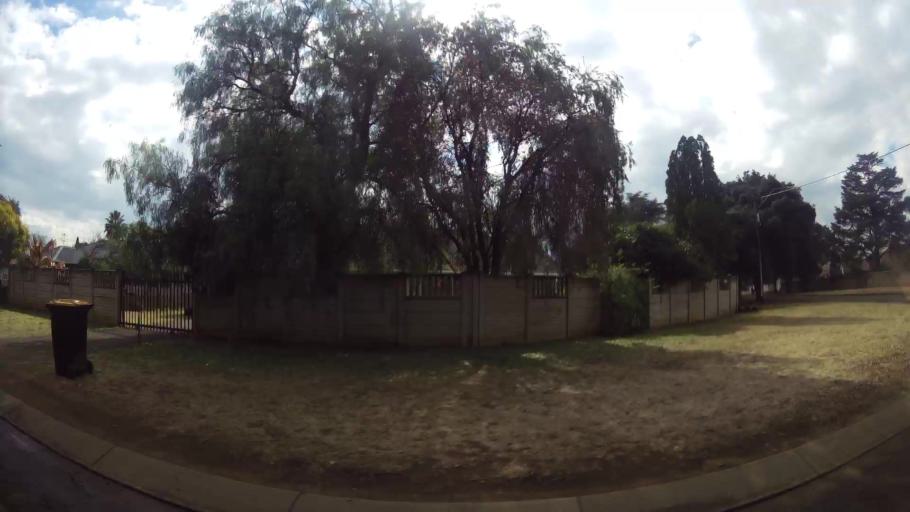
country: ZA
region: Gauteng
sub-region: Sedibeng District Municipality
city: Vereeniging
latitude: -26.6506
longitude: 27.9713
